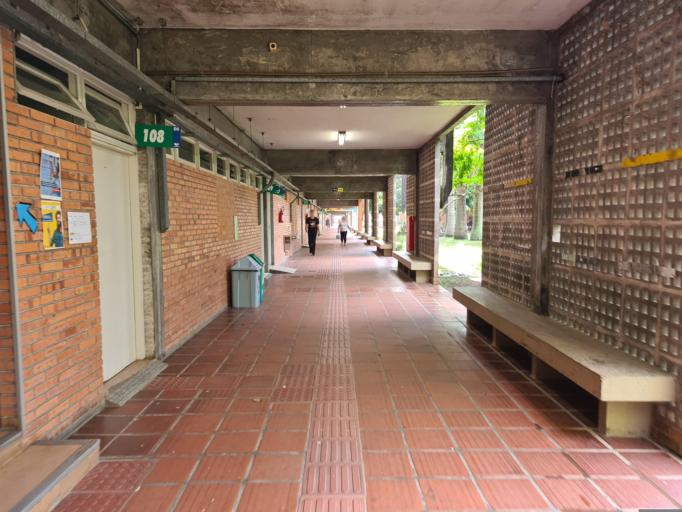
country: BR
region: Santa Catarina
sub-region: Itajai
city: Itajai
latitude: -26.9147
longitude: -48.6619
